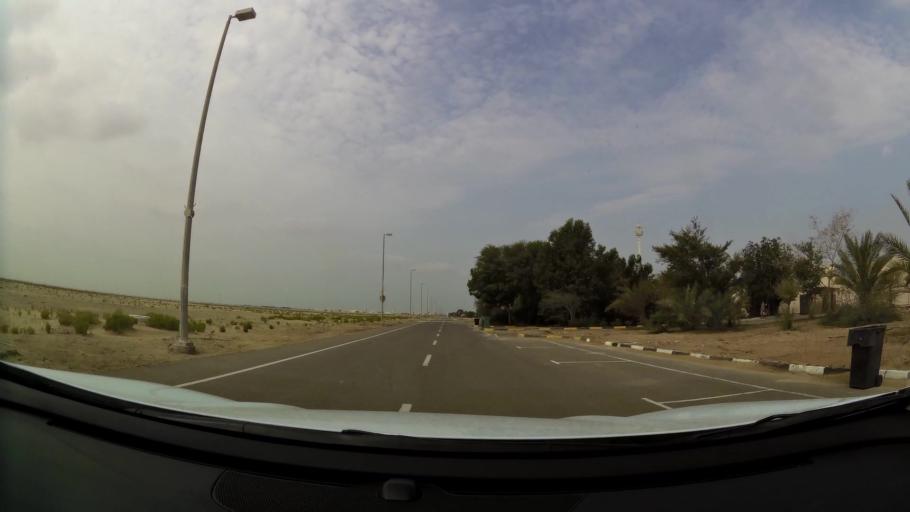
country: AE
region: Abu Dhabi
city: Abu Dhabi
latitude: 24.6322
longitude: 54.6804
